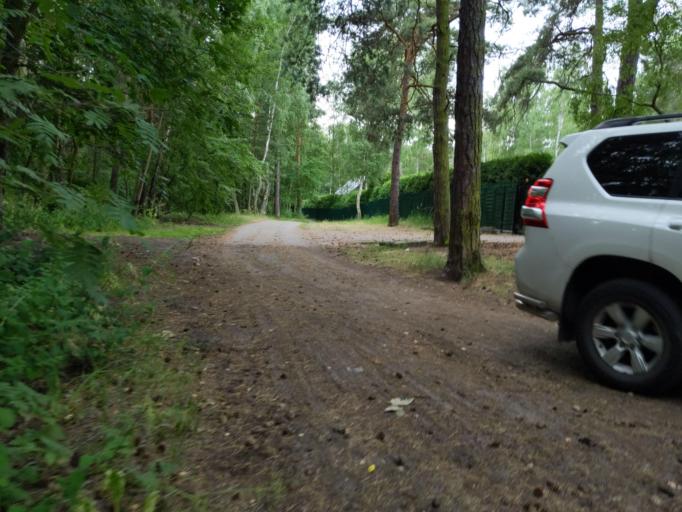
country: PL
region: Pomeranian Voivodeship
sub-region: Gdansk
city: Gdansk
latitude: 54.3705
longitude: 18.7334
